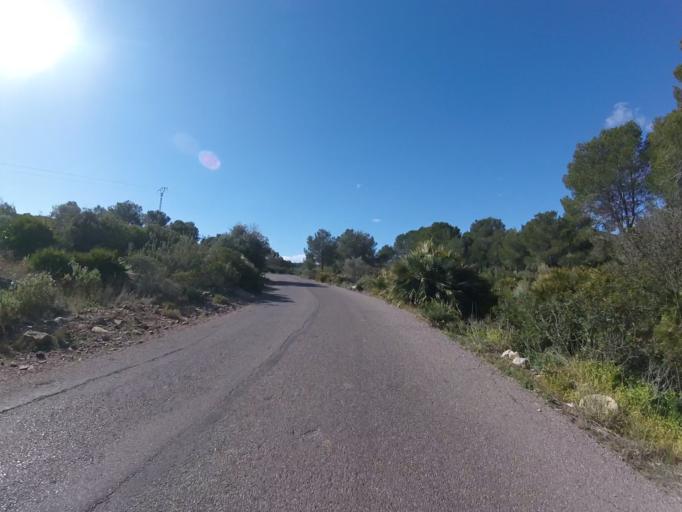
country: ES
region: Valencia
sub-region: Provincia de Castello
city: Orpesa/Oropesa del Mar
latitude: 40.0875
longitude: 0.1249
